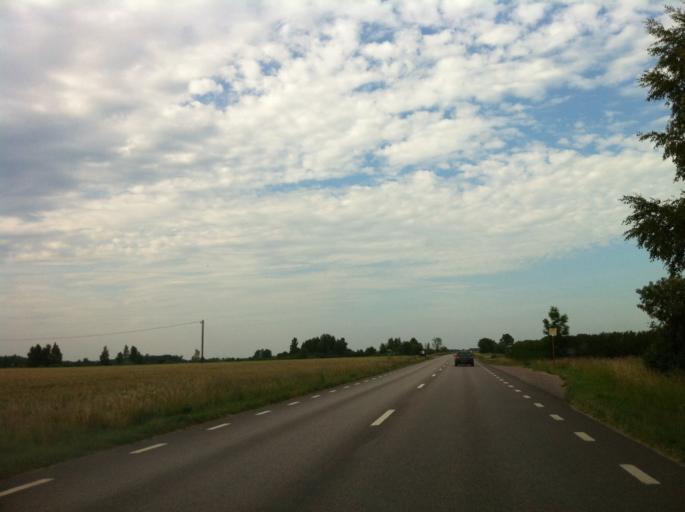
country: SE
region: Kalmar
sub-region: Borgholms Kommun
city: Borgholm
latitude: 56.9704
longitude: 16.8033
